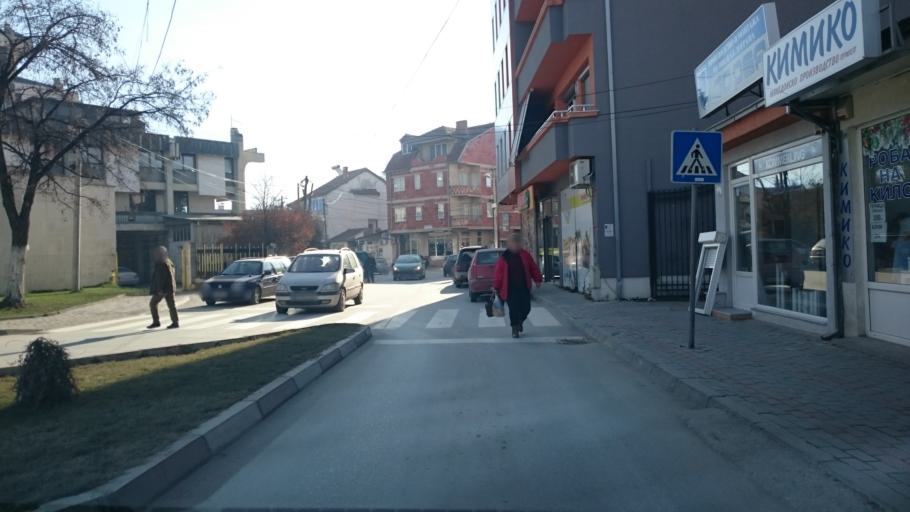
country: MK
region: Prilep
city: Prilep
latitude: 41.3477
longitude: 21.5517
